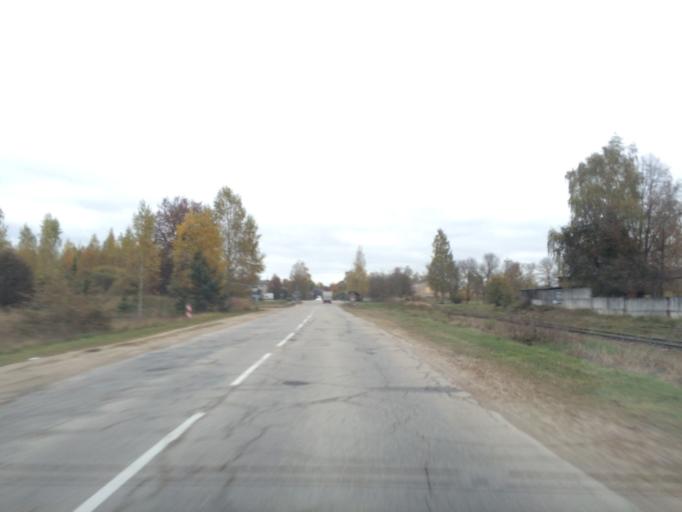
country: LV
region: Plavinu
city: Plavinas
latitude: 56.6097
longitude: 25.6901
